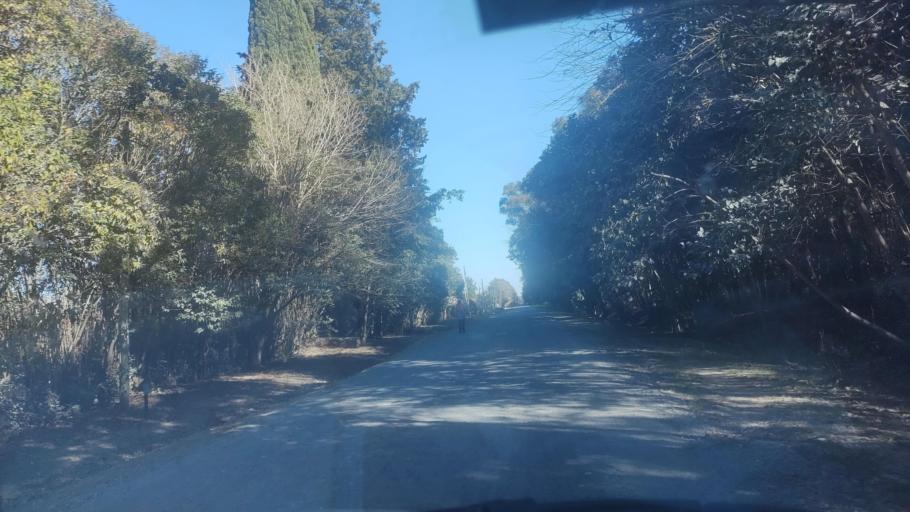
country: AR
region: Buenos Aires
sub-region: Partido de La Plata
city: La Plata
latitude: -34.8487
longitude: -58.1004
